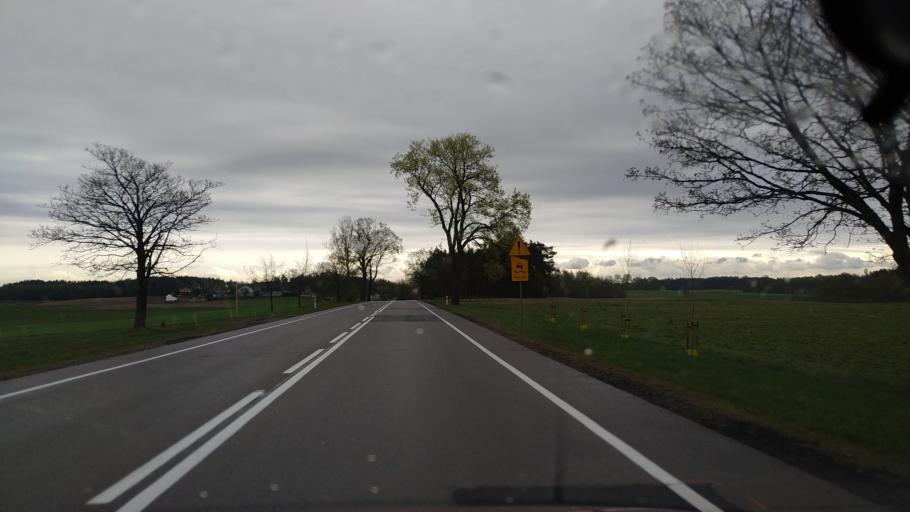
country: PL
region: Pomeranian Voivodeship
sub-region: Powiat chojnicki
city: Czersk
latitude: 53.8047
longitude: 18.0130
